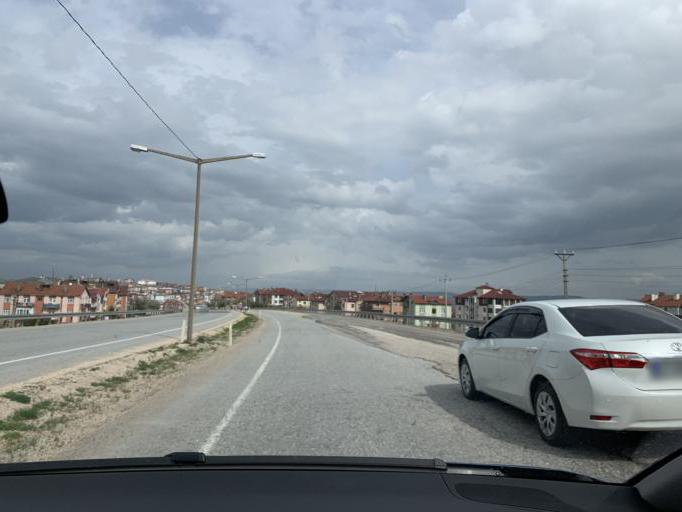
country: TR
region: Bolu
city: Gerede
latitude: 40.7963
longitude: 32.1929
